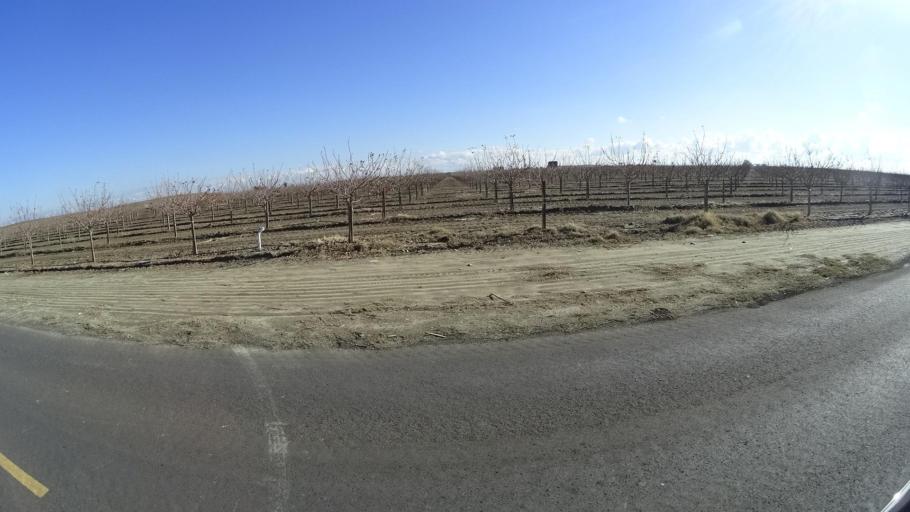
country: US
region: California
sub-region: Kern County
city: Delano
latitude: 35.7362
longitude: -119.2584
